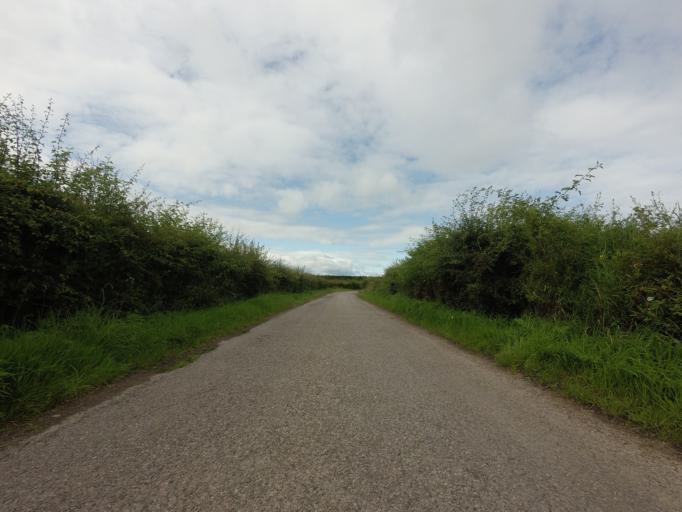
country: GB
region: Scotland
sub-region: Moray
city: Hopeman
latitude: 57.6702
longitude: -3.3874
